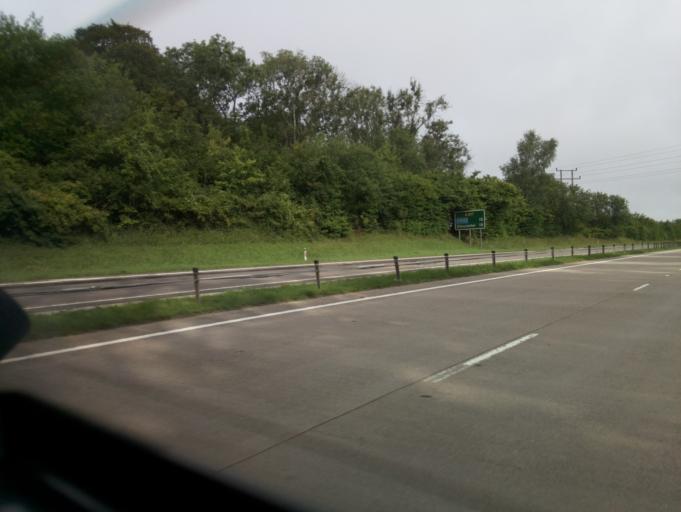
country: GB
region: England
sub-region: Gloucestershire
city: Cirencester
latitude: 51.7272
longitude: -1.9514
